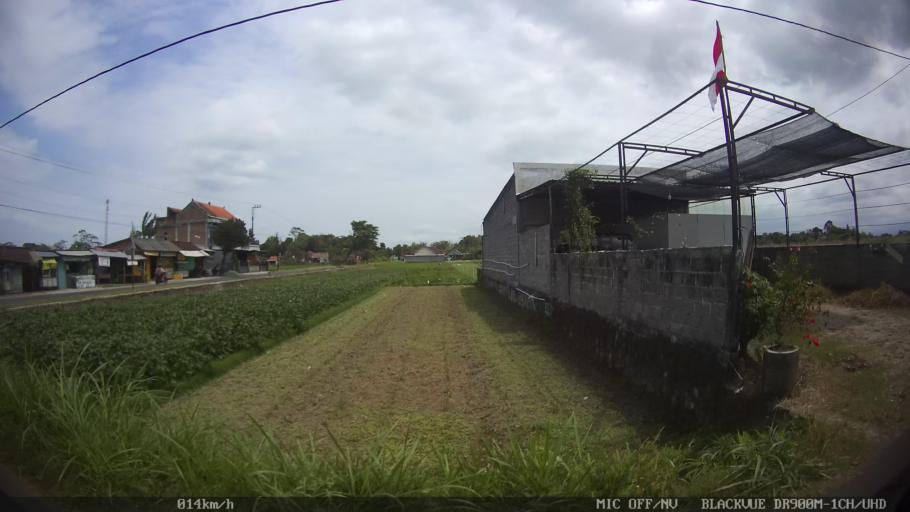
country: ID
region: Central Java
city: Candi Prambanan
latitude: -7.8147
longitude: 110.4999
